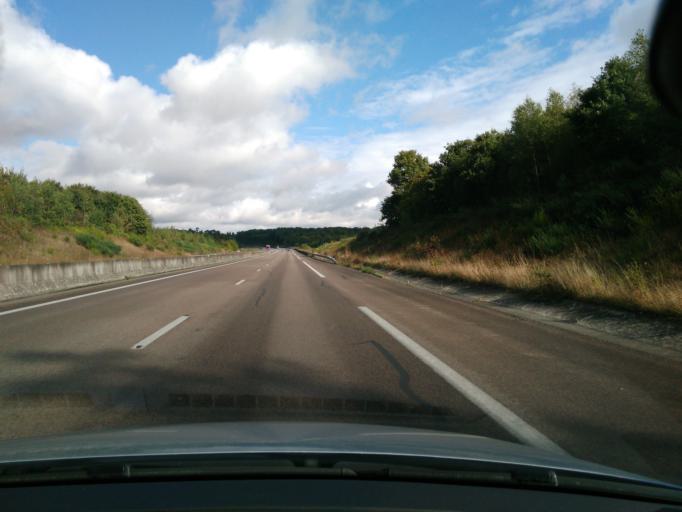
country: FR
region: Haute-Normandie
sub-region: Departement de l'Eure
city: La Madeleine-de-Nonancourt
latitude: 48.8097
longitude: 1.1915
